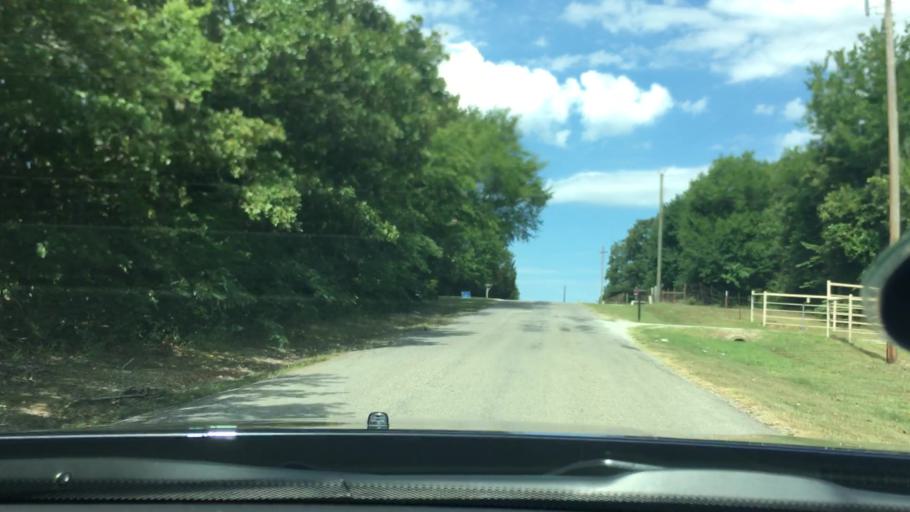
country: US
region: Oklahoma
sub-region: Pontotoc County
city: Ada
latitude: 34.7635
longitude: -96.5796
